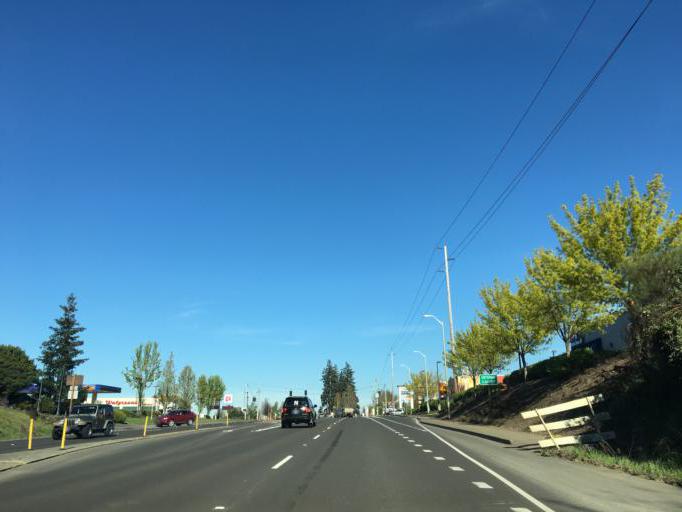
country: US
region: Oregon
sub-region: Clackamas County
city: Canby
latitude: 45.2558
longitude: -122.7061
